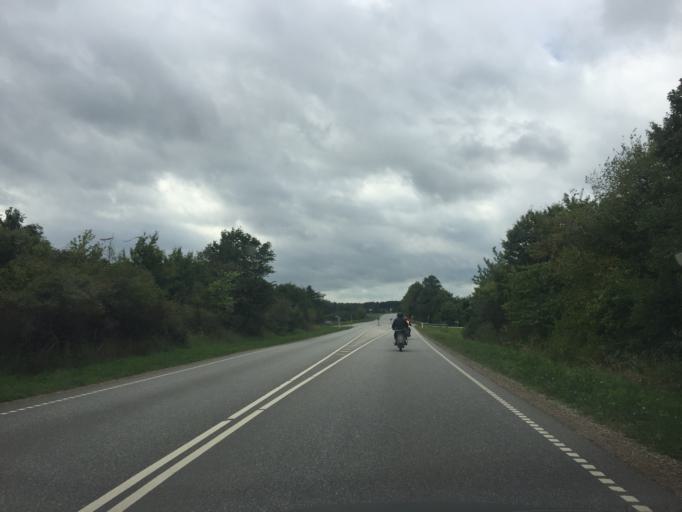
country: DK
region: Capital Region
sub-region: Hillerod Kommune
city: Skaevinge
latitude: 55.9368
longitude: 12.1164
